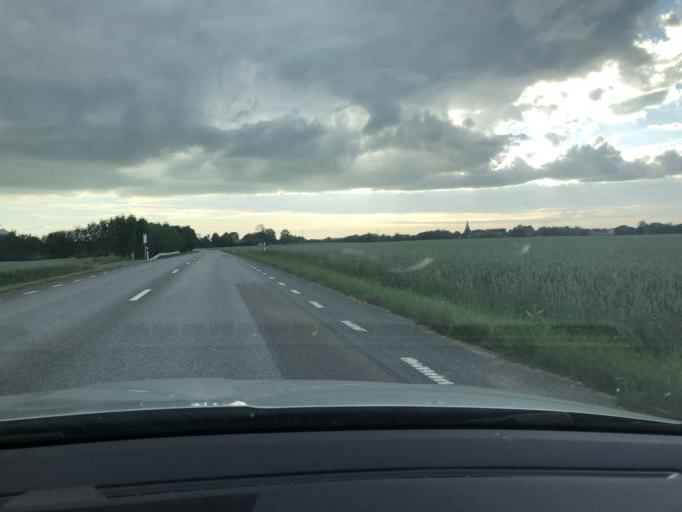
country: SE
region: Skane
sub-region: Simrishamns Kommun
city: Simrishamn
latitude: 55.5291
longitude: 14.2557
